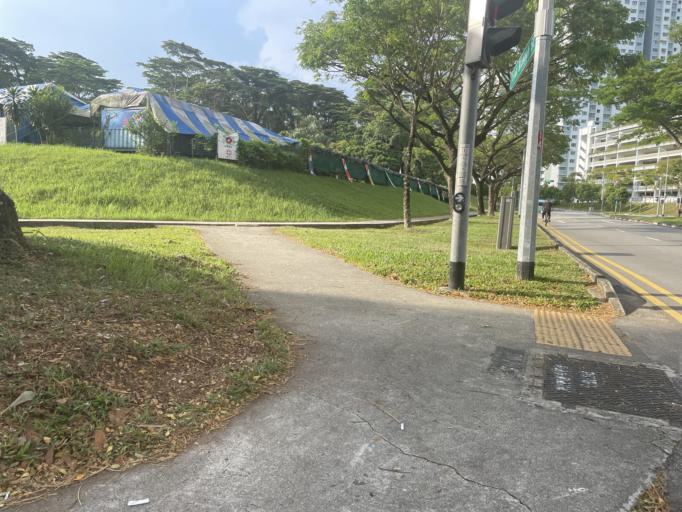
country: SG
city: Singapore
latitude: 1.2736
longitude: 103.8061
